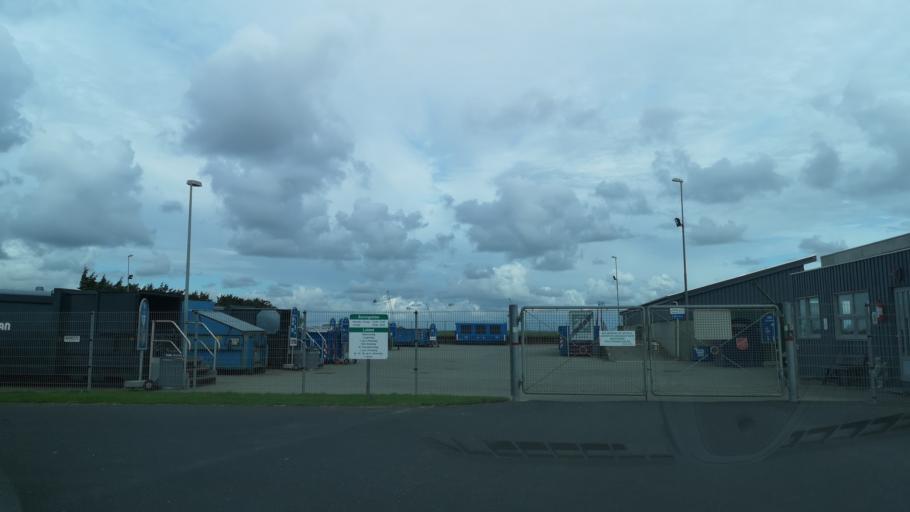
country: DK
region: Central Jutland
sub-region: Ringkobing-Skjern Kommune
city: Hvide Sande
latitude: 56.0153
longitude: 8.1290
